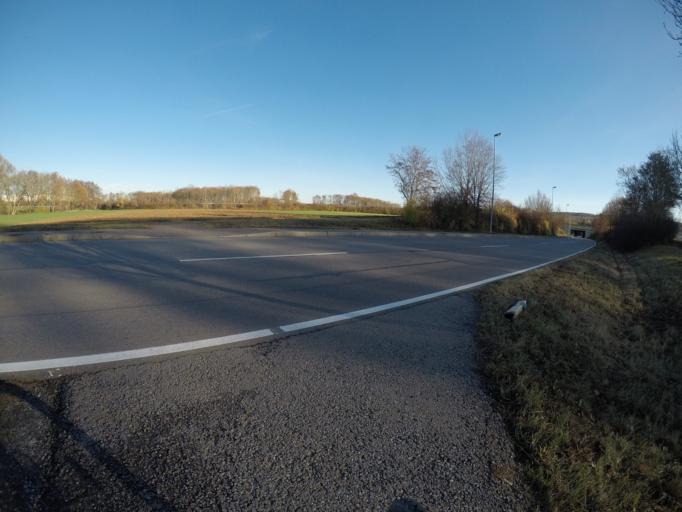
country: DE
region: Baden-Wuerttemberg
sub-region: Regierungsbezirk Stuttgart
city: Ehningen
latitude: 48.6825
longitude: 8.9653
